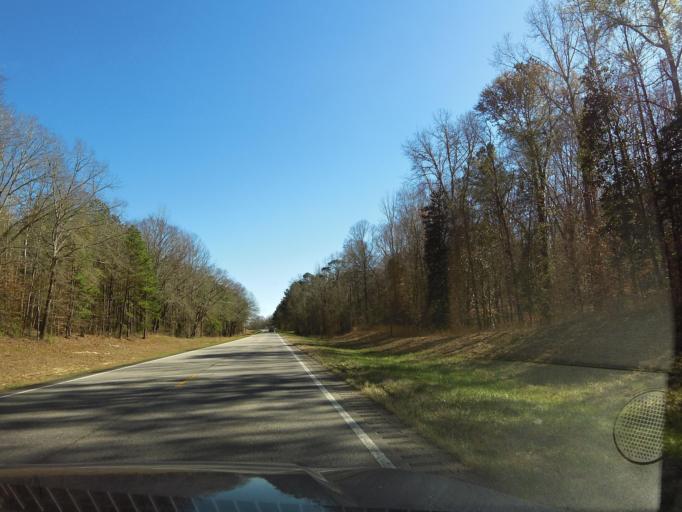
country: US
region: Alabama
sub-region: Bullock County
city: Union Springs
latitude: 32.1034
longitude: -85.5739
